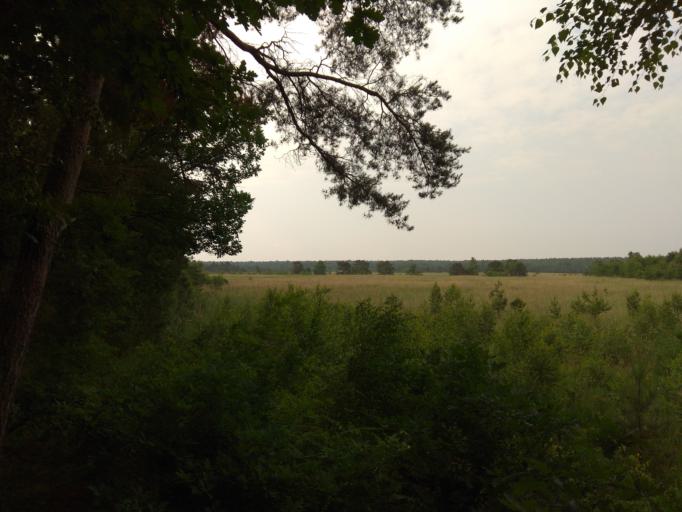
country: DE
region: Saxony
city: Doberschutz
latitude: 51.5545
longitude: 12.7582
